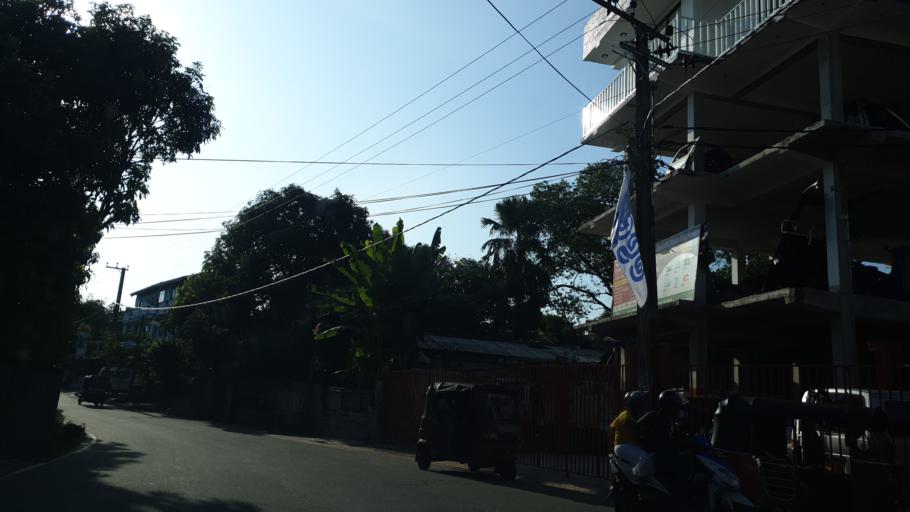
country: LK
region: Western
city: Galkissa
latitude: 6.8522
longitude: 79.8823
